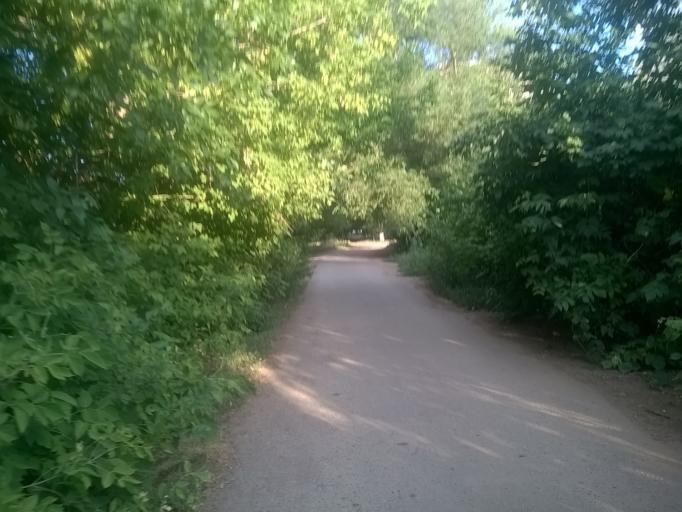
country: RU
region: Rostov
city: Donetsk
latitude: 48.3323
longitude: 39.9605
